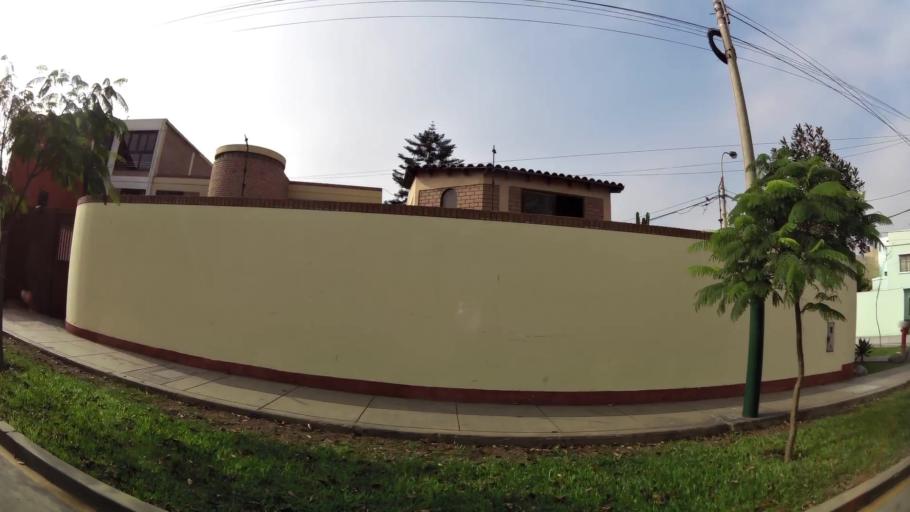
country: PE
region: Lima
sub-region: Lima
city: San Isidro
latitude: -12.0963
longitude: -77.0630
